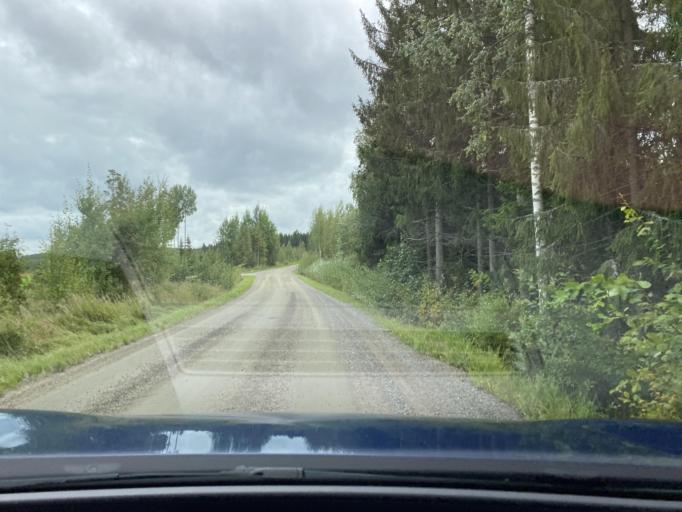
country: FI
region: Pirkanmaa
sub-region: Lounais-Pirkanmaa
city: Punkalaidun
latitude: 61.2209
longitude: 23.1624
